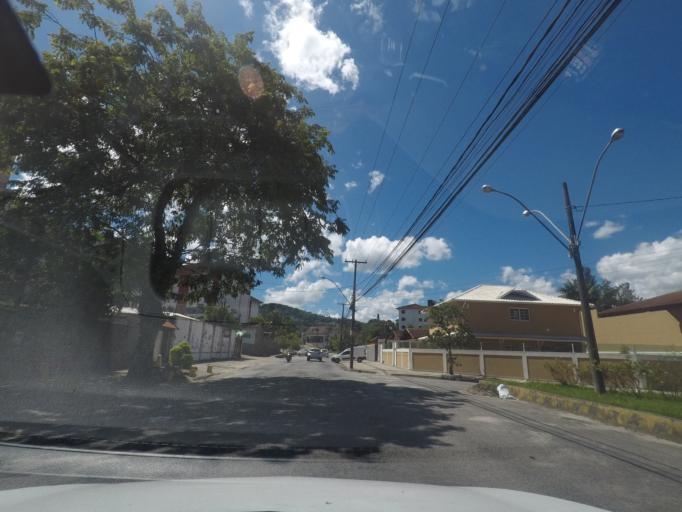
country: BR
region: Rio de Janeiro
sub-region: Teresopolis
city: Teresopolis
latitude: -22.4327
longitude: -42.9777
